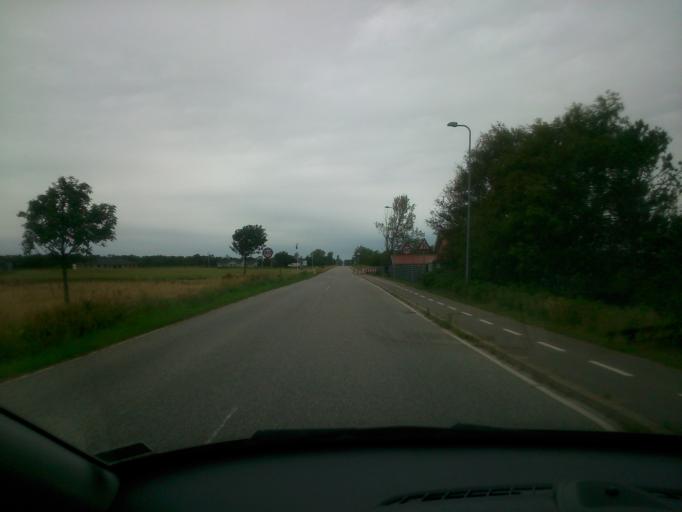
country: DK
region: Central Jutland
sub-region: Ringkobing-Skjern Kommune
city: Skjern
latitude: 55.9574
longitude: 8.4830
